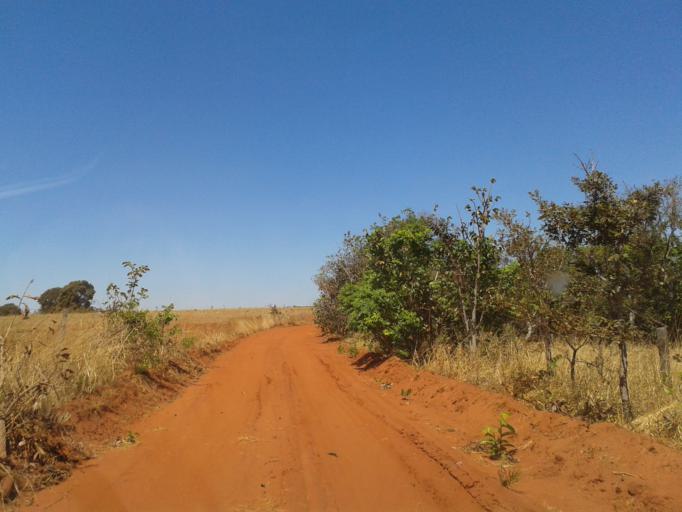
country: BR
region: Minas Gerais
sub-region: Ituiutaba
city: Ituiutaba
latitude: -19.1031
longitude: -49.2707
